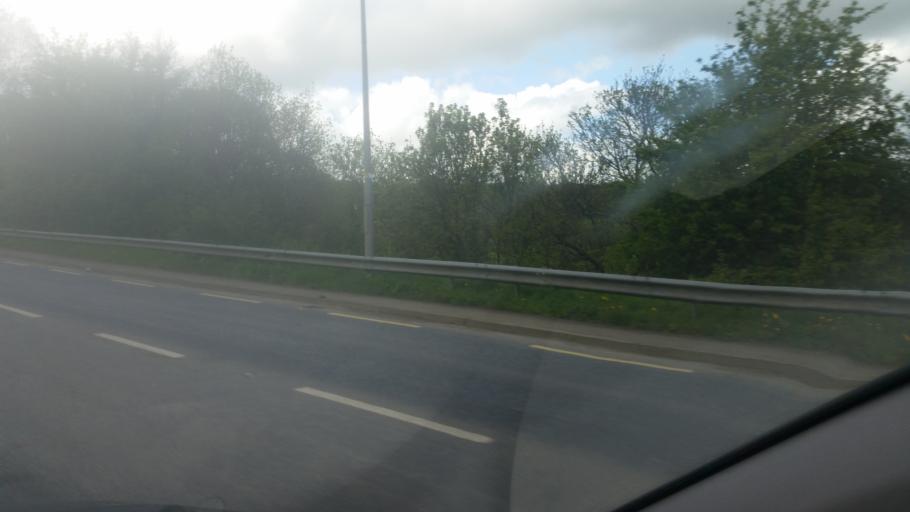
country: IE
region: Leinster
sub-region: Loch Garman
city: Enniscorthy
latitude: 52.4918
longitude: -6.5654
